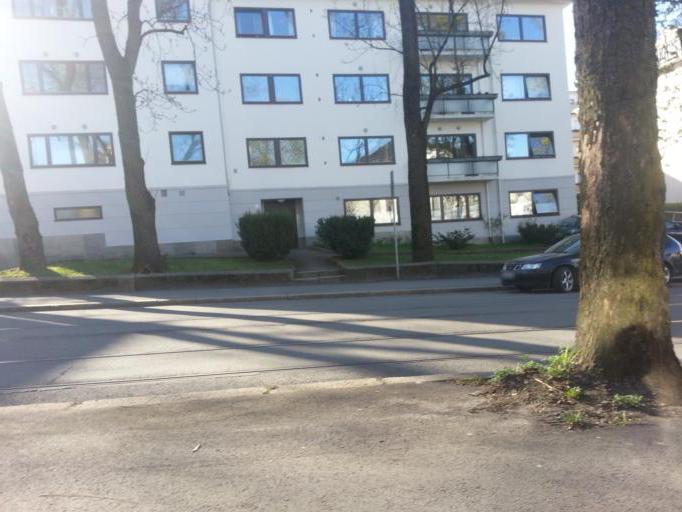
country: NO
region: Oslo
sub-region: Oslo
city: Oslo
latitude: 59.9133
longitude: 10.7131
